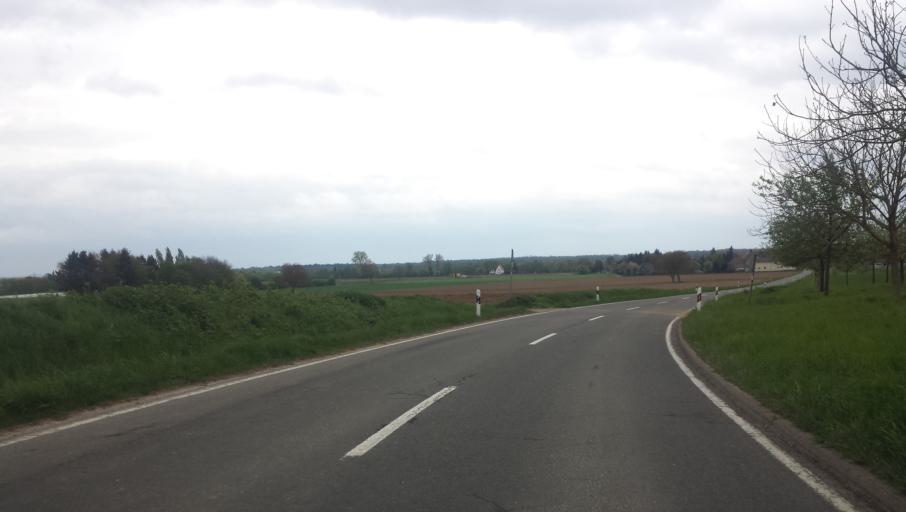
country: DE
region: Rheinland-Pfalz
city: Westheim
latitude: 49.2573
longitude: 8.3248
